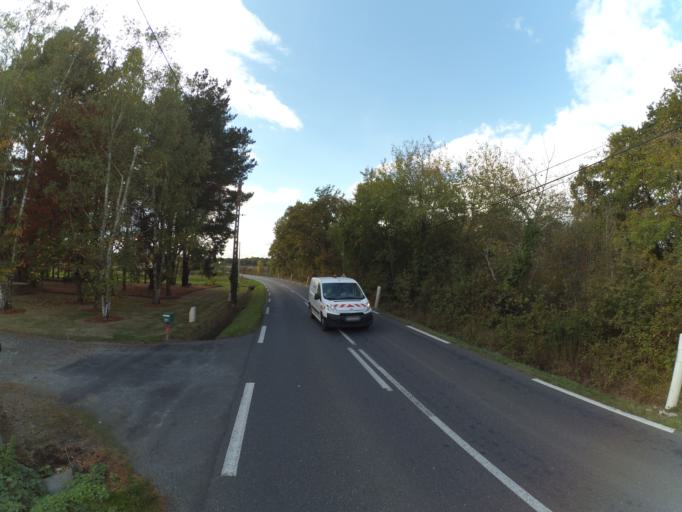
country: FR
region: Pays de la Loire
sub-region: Departement de la Loire-Atlantique
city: Saint-Lumine-de-Clisson
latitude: 47.0804
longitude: -1.3459
